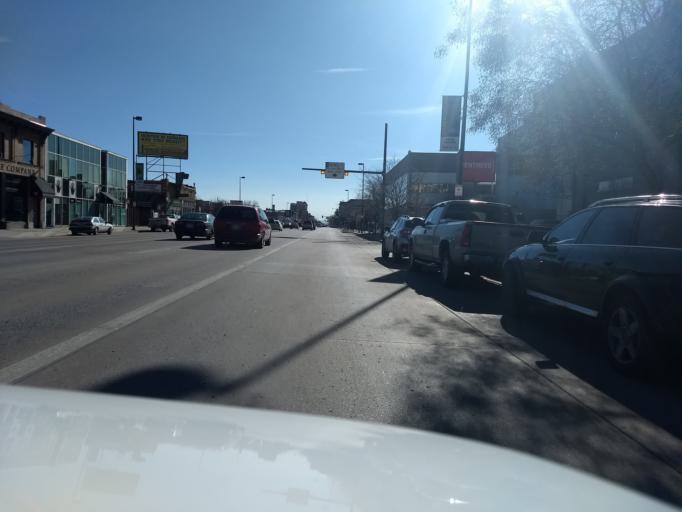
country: US
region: Colorado
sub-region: Denver County
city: Denver
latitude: 39.7234
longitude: -104.9876
